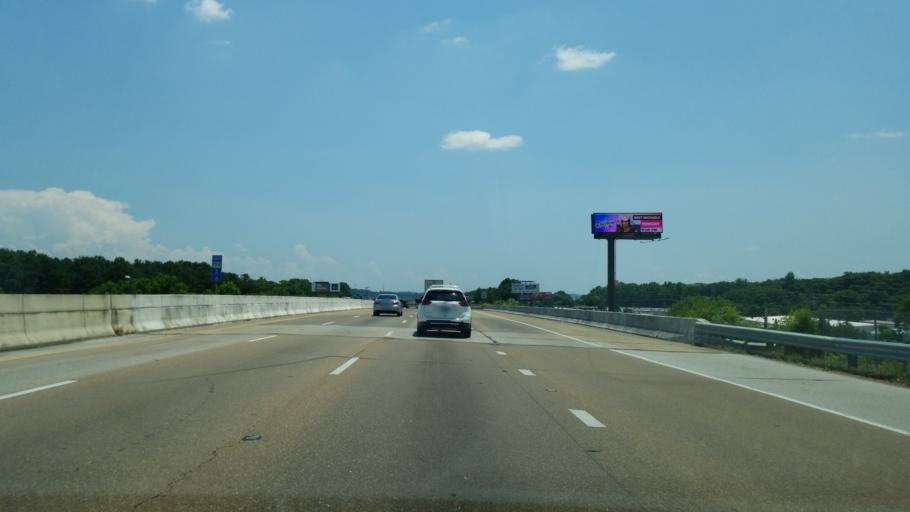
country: US
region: Tennessee
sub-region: Hamilton County
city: East Chattanooga
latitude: 35.0701
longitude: -85.1970
